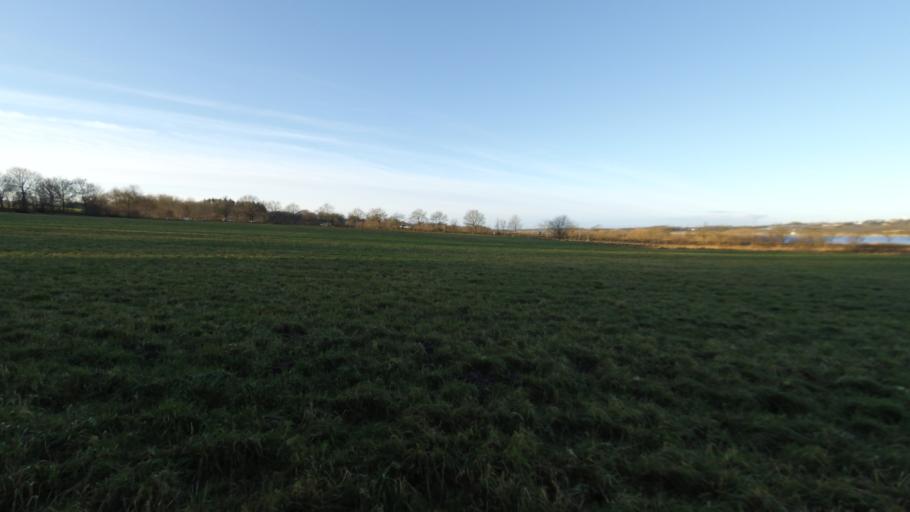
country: DK
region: Central Jutland
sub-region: Arhus Kommune
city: Stavtrup
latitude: 56.1417
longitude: 10.0922
